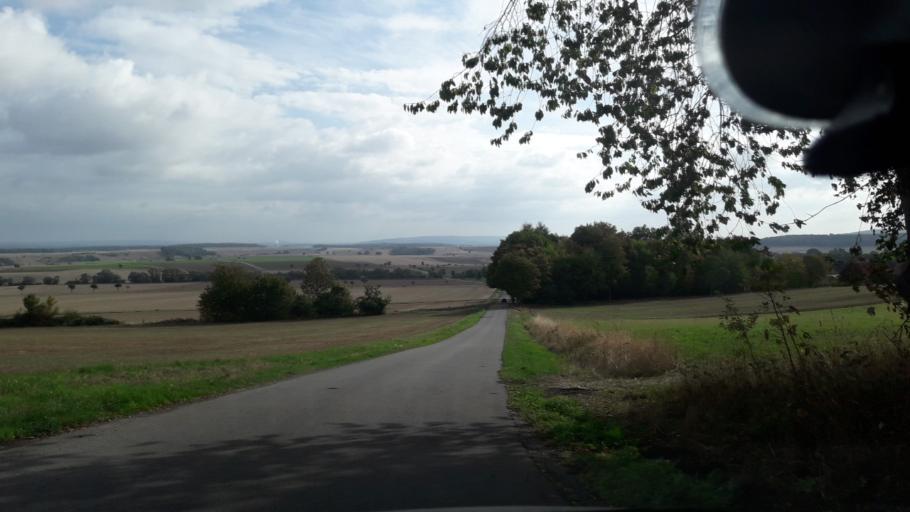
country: DE
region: Lower Saxony
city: Liebenburg
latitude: 52.0012
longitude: 10.4318
